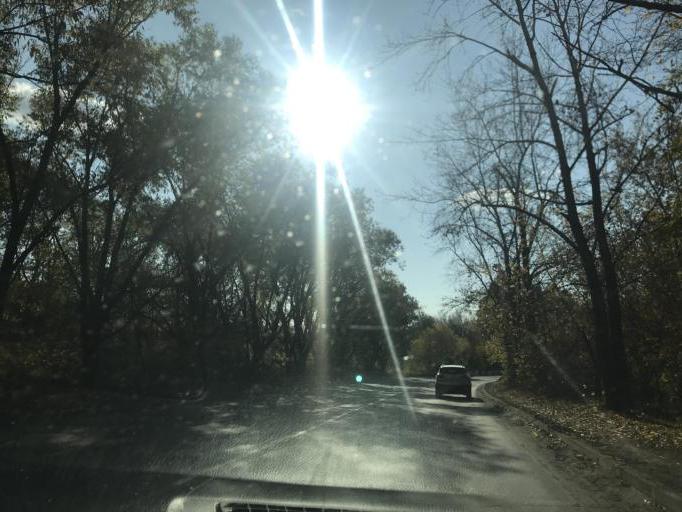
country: RU
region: Chelyabinsk
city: Dolgoderevenskoye
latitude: 55.2558
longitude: 61.3576
